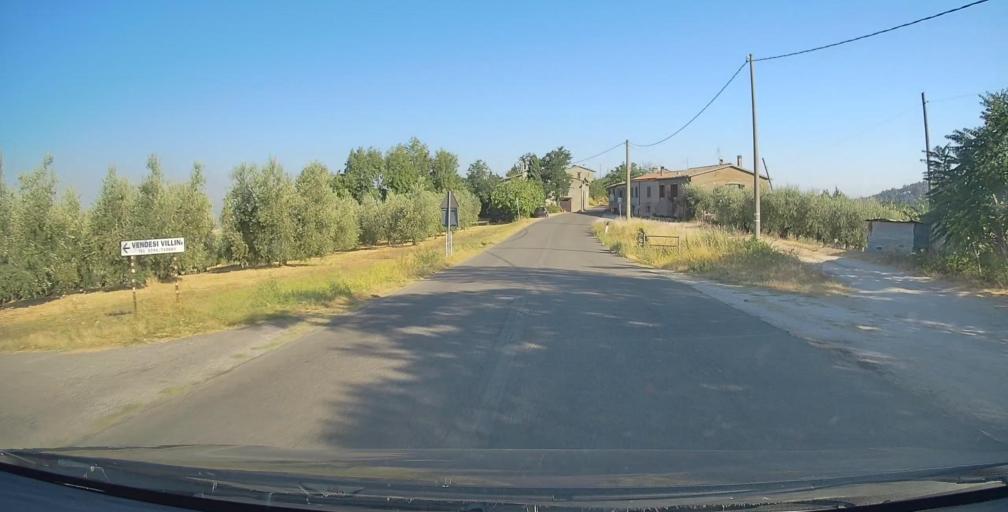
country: IT
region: Umbria
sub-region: Provincia di Terni
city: Calvi dell'Umbria
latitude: 42.4095
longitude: 12.5584
